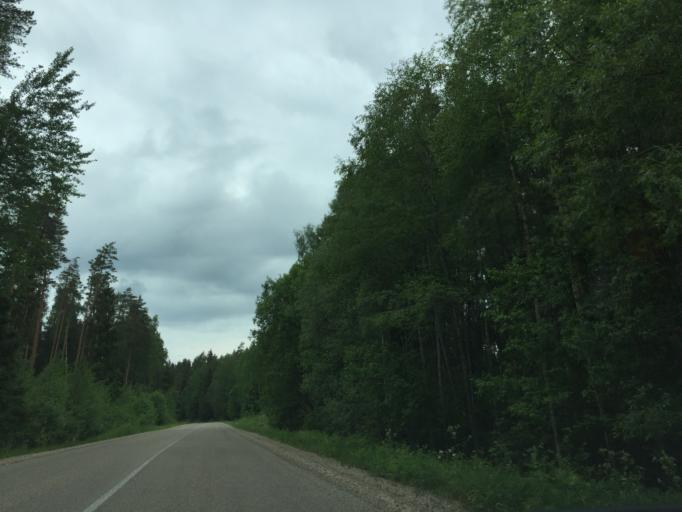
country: LV
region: Varkava
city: Vecvarkava
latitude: 56.0757
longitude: 26.6278
